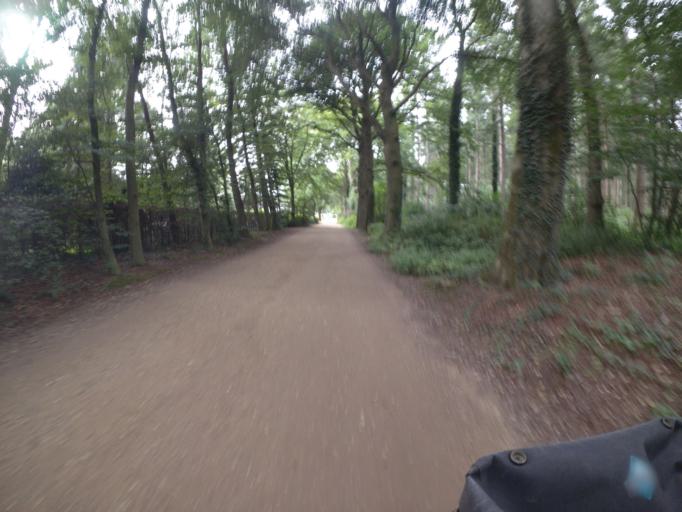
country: NL
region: Gelderland
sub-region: Gemeente Groesbeek
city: Groesbeek
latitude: 51.7633
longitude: 5.9097
